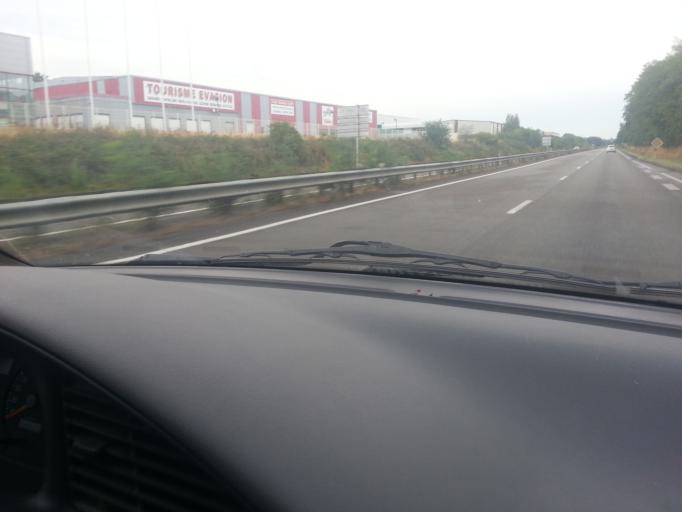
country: FR
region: Bourgogne
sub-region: Departement de Saone-et-Loire
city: Montceau-les-Mines
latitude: 46.6883
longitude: 4.3630
